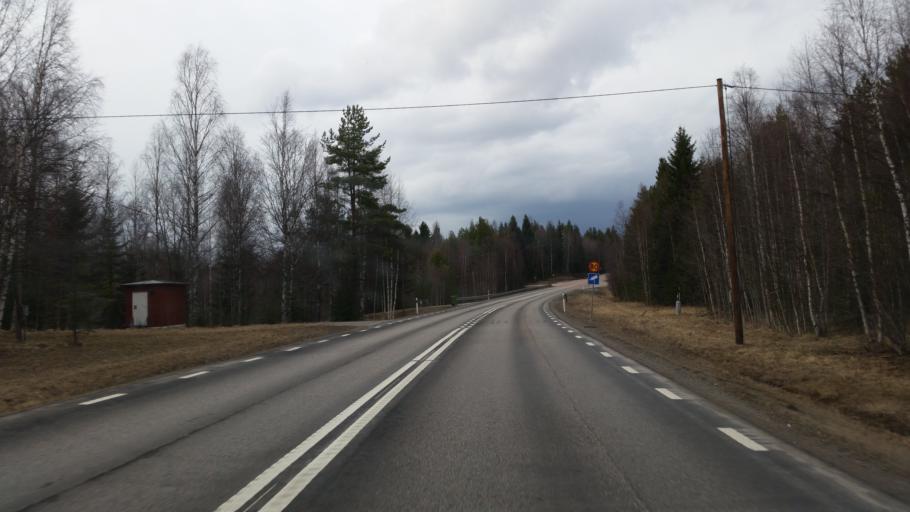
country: SE
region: Gaevleborg
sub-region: Ljusdals Kommun
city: Ljusdal
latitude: 61.7868
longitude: 16.1318
